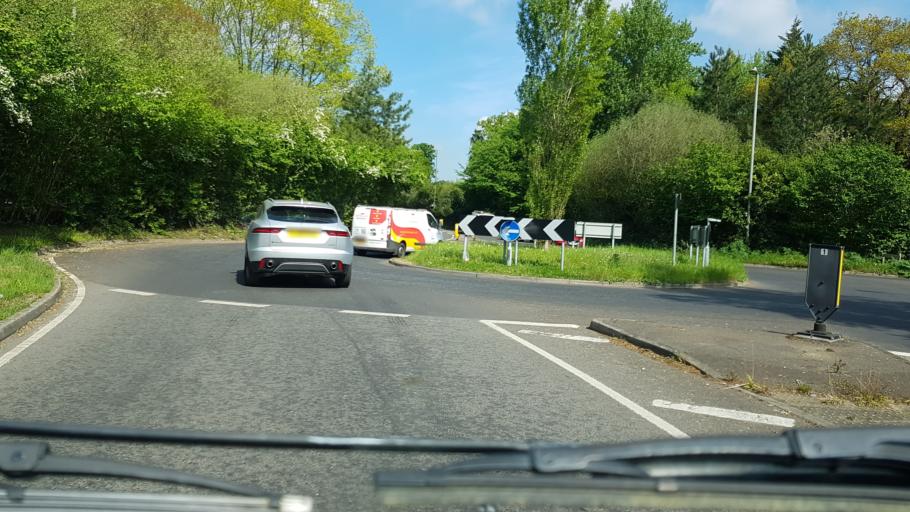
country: GB
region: England
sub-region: Surrey
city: Leatherhead
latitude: 51.3195
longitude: -0.3418
